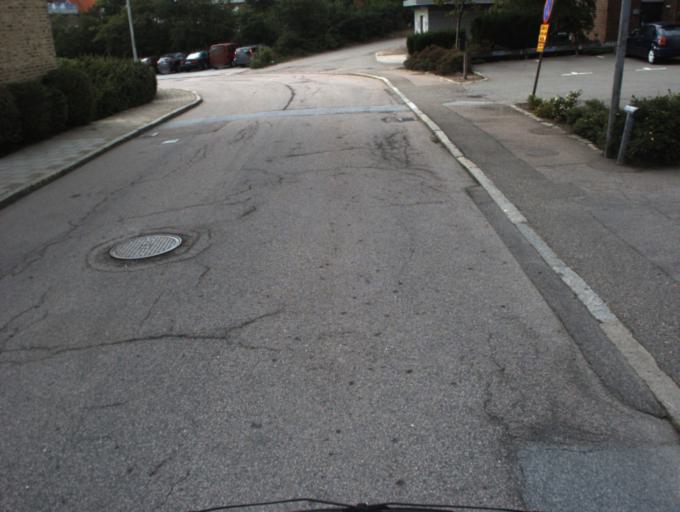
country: SE
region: Skane
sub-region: Helsingborg
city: Helsingborg
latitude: 56.0610
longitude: 12.6996
